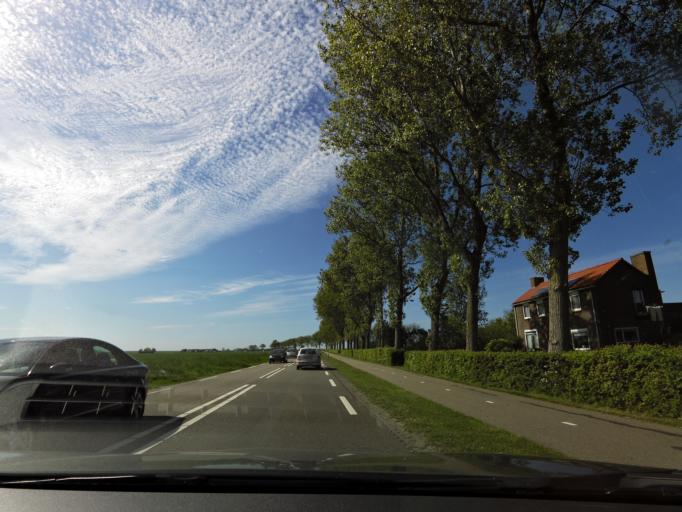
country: NL
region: Zeeland
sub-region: Schouwen-Duiveland
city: Scharendijke
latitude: 51.6561
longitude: 3.9115
